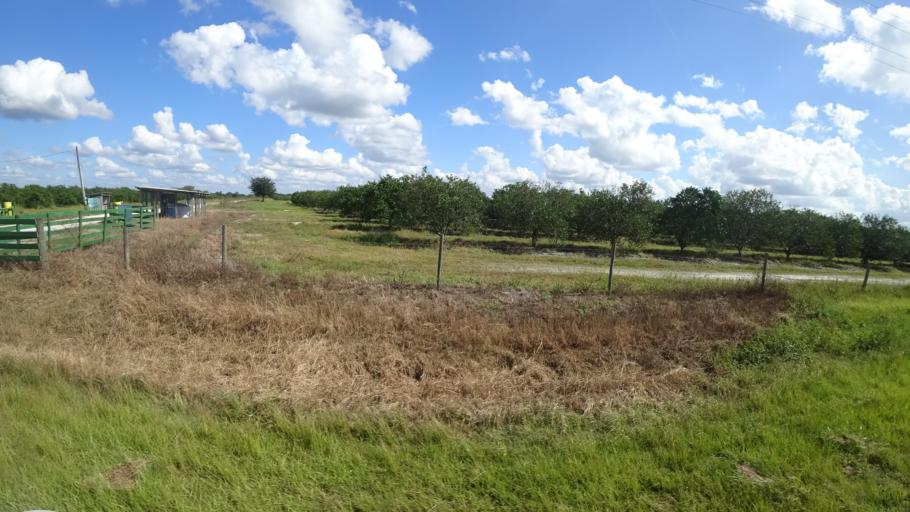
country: US
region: Florida
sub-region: Sarasota County
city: Lake Sarasota
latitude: 27.3937
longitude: -82.1335
